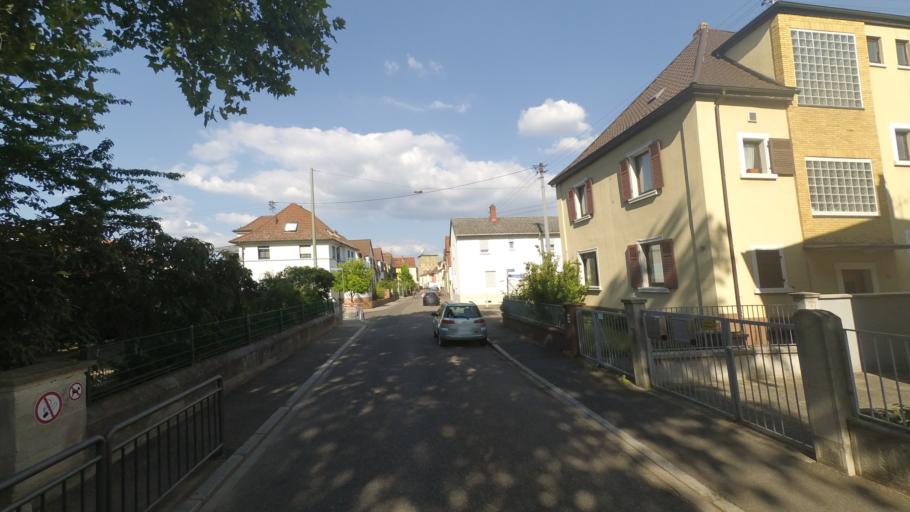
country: DE
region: Rheinland-Pfalz
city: Frankenthal
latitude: 49.5206
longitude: 8.3995
